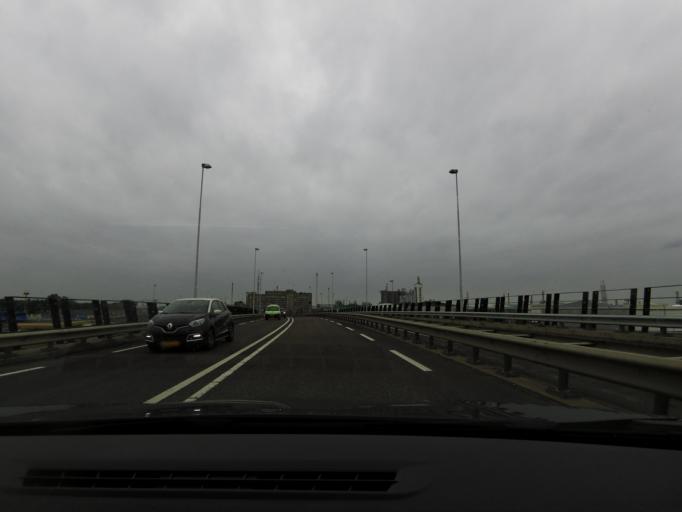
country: NL
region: South Holland
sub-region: Gemeente Vlaardingen
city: Vlaardingen
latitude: 51.8772
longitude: 4.3632
